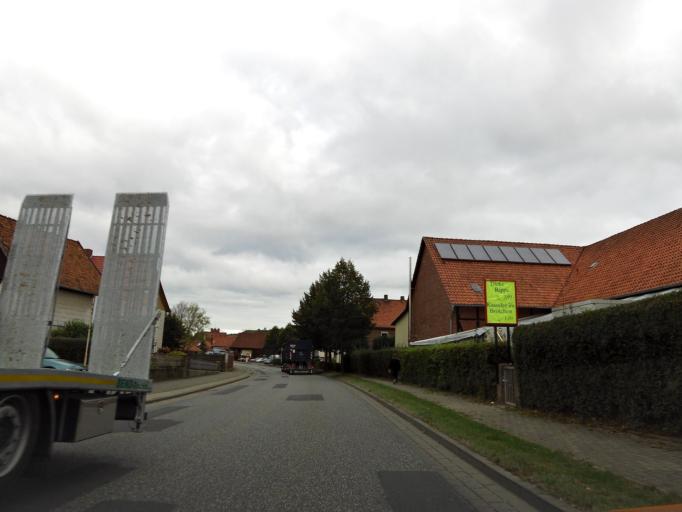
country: DE
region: Lower Saxony
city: Northeim
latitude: 51.7648
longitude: 9.9594
